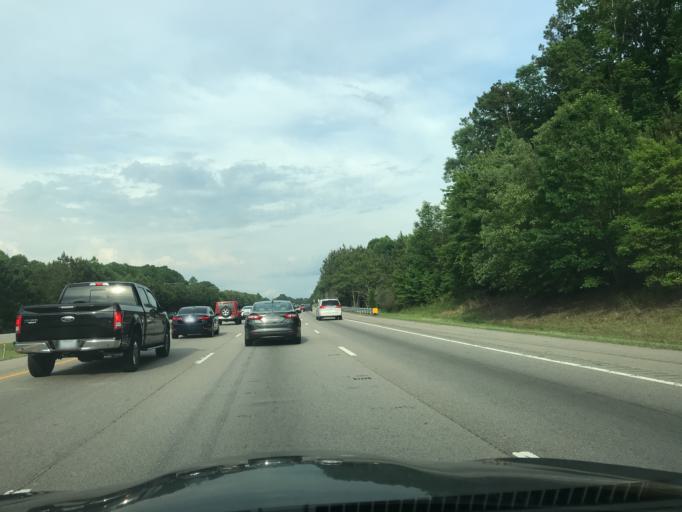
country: US
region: North Carolina
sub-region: Wake County
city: West Raleigh
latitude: 35.9157
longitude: -78.7032
